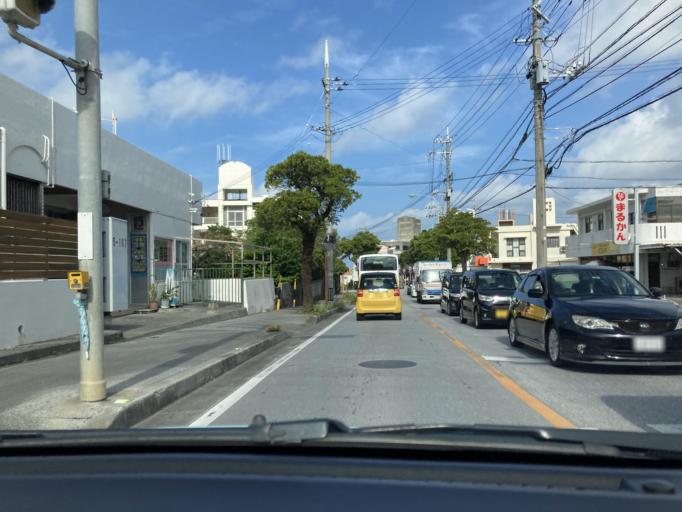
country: JP
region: Okinawa
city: Ginowan
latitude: 26.2592
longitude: 127.7649
